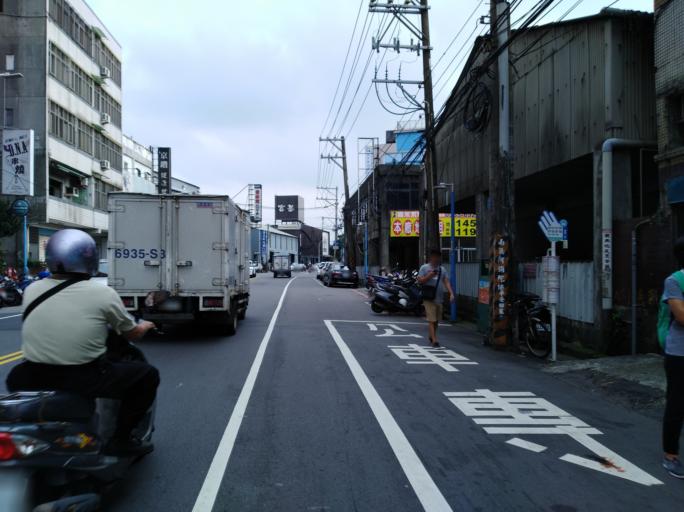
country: TW
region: Taipei
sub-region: Taipei
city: Banqiao
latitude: 25.0300
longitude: 121.4345
